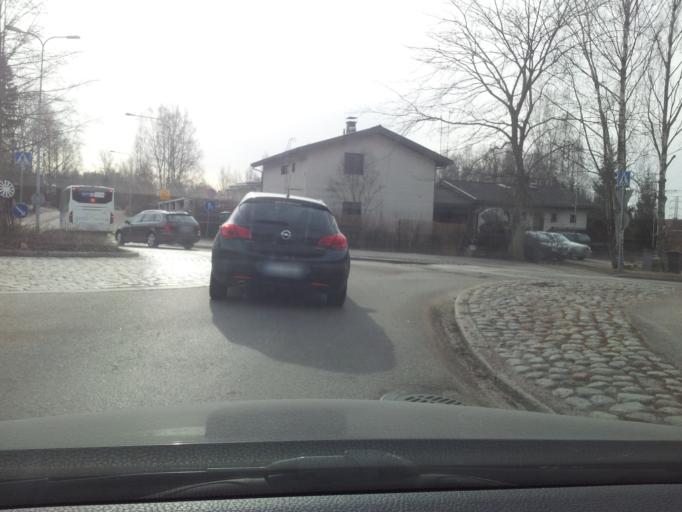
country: FI
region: Uusimaa
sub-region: Helsinki
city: Kilo
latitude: 60.1907
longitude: 24.7772
